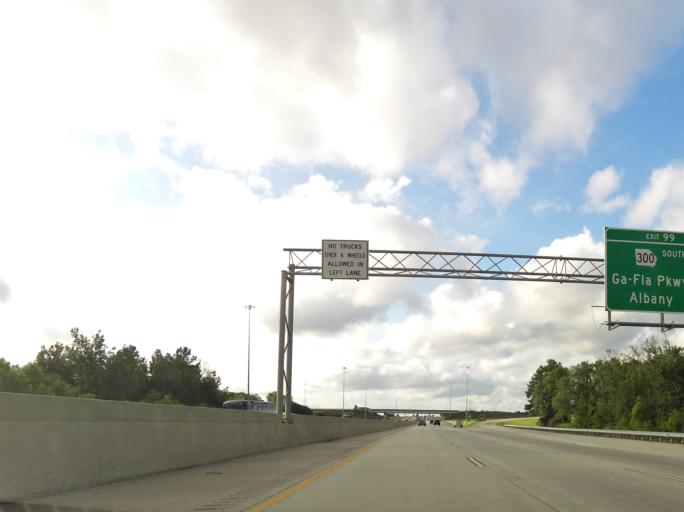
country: US
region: Georgia
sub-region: Crisp County
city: Cordele
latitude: 31.9302
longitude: -83.7468
